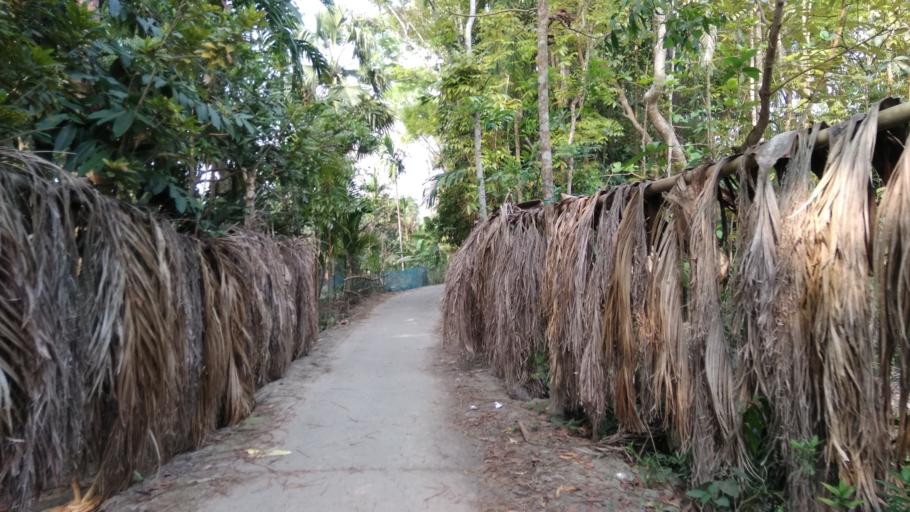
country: BD
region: Barisal
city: Mehendiganj
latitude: 22.9500
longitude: 90.4146
